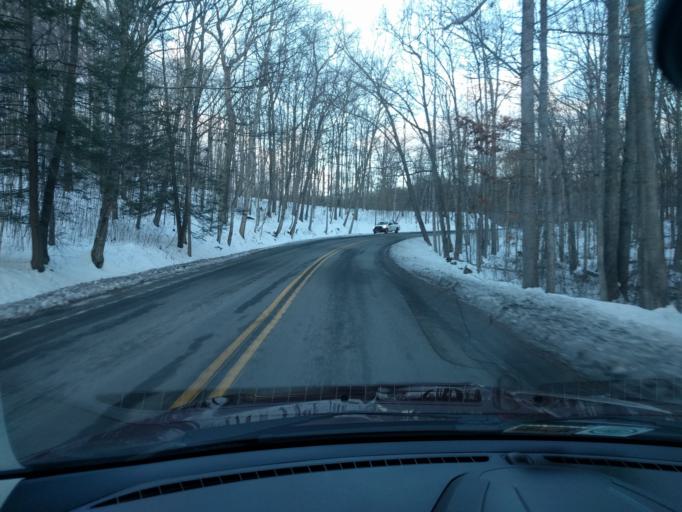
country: US
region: Virginia
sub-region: Bath County
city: Warm Springs
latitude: 38.0975
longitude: -79.8469
